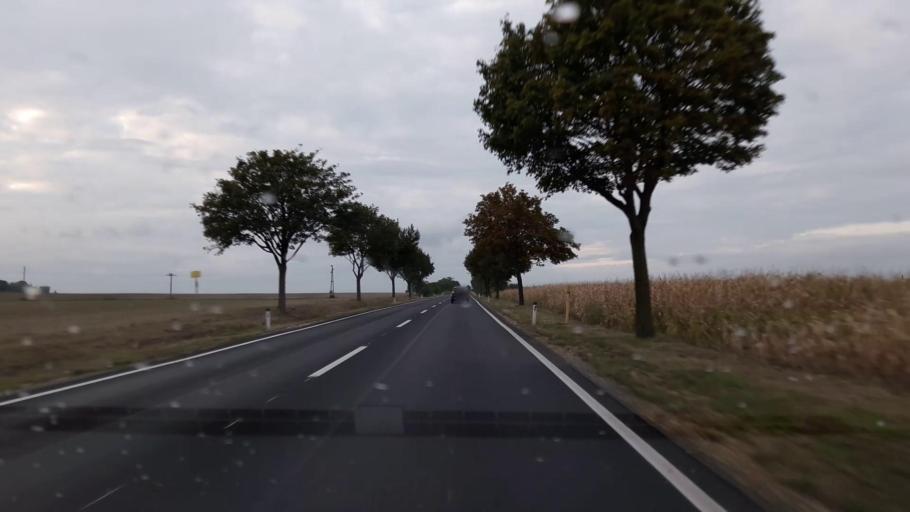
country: AT
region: Lower Austria
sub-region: Politischer Bezirk Wien-Umgebung
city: Schwadorf
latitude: 48.0800
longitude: 16.5698
